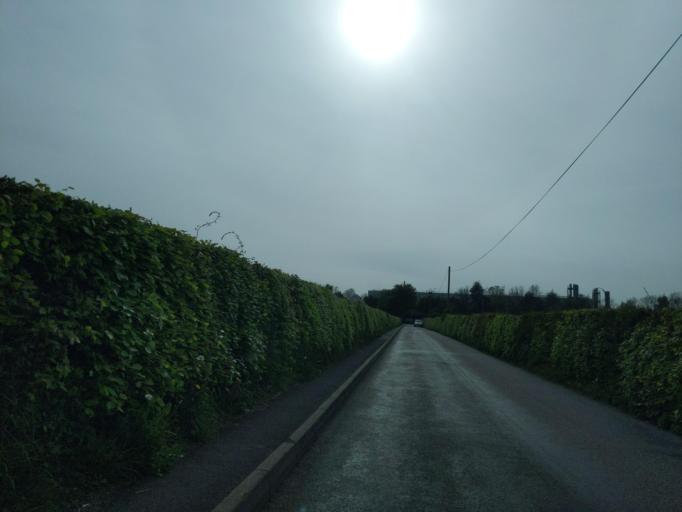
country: GB
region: England
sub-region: Devon
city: Yelverton
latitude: 50.4436
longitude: -4.1060
